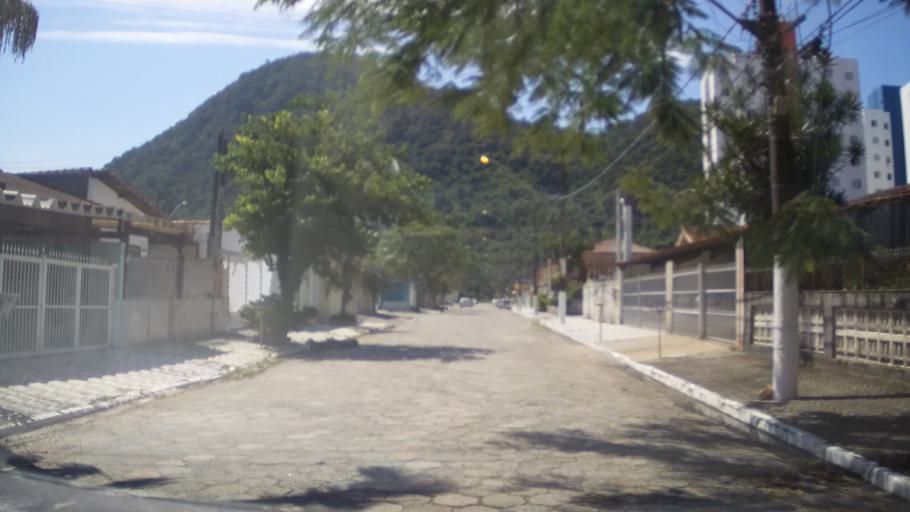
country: BR
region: Sao Paulo
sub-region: Praia Grande
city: Praia Grande
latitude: -24.0100
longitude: -46.3984
